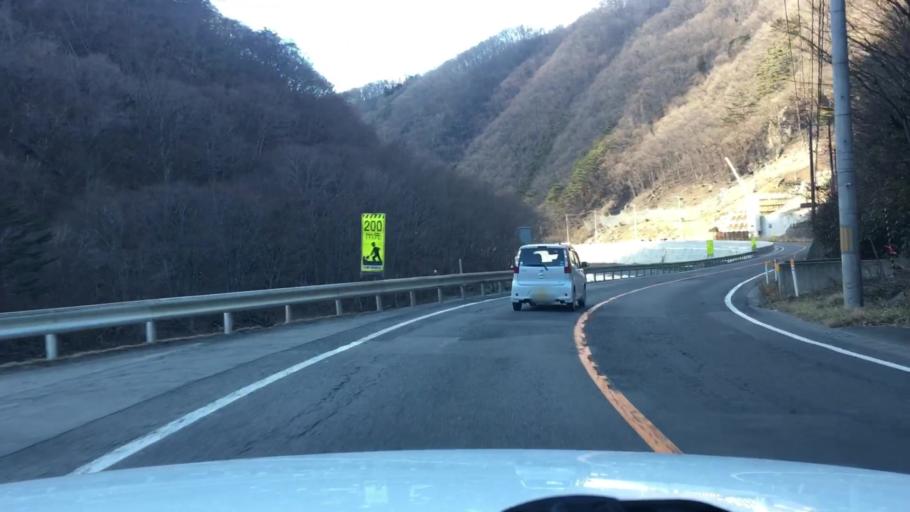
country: JP
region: Iwate
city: Miyako
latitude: 39.5975
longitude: 141.7597
